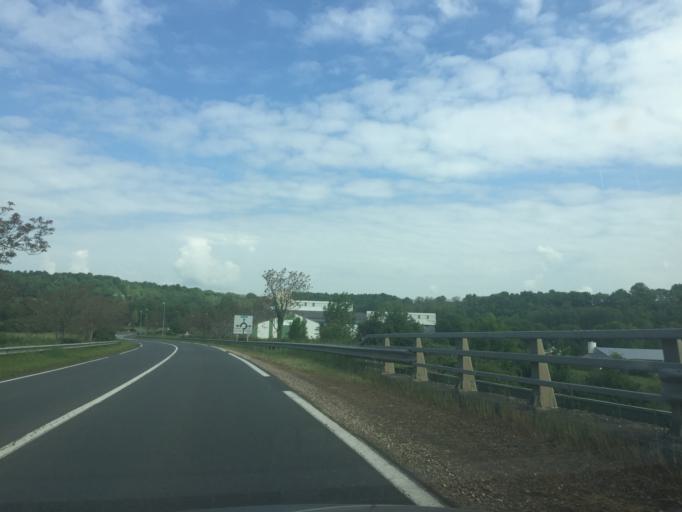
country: FR
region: Poitou-Charentes
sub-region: Departement de la Vienne
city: Lusignan
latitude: 46.4451
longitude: 0.1394
